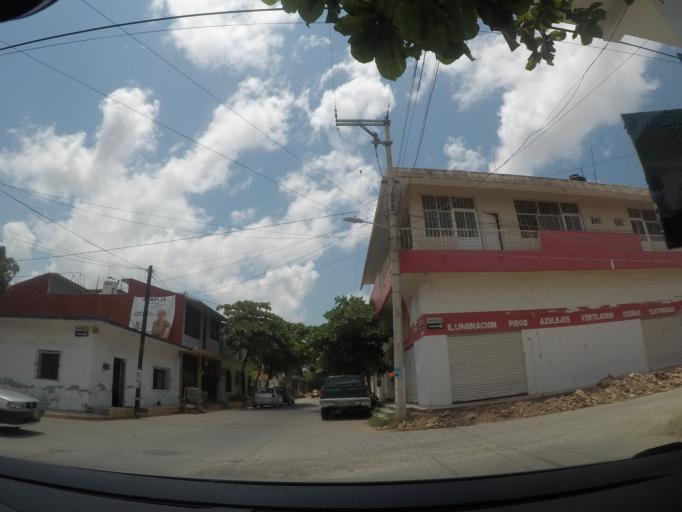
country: MX
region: Oaxaca
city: Juchitan de Zaragoza
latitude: 16.4407
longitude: -95.0230
